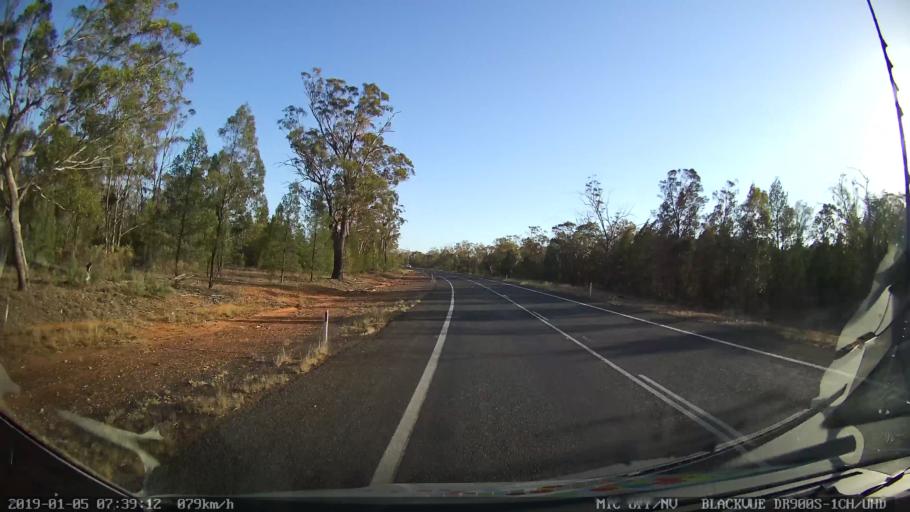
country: AU
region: New South Wales
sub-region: Gilgandra
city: Gilgandra
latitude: -31.9400
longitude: 148.6186
